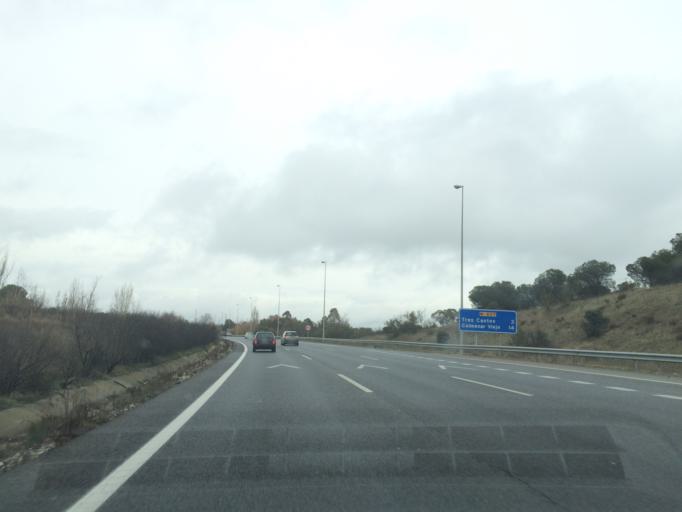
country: ES
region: Madrid
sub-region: Provincia de Madrid
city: Tres Cantos
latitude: 40.5649
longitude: -3.7104
